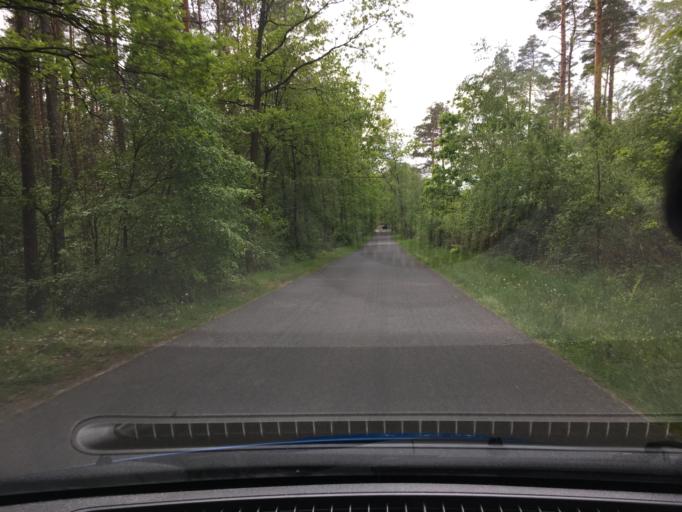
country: DE
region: Lower Saxony
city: Rehlingen
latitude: 53.1024
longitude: 10.2309
